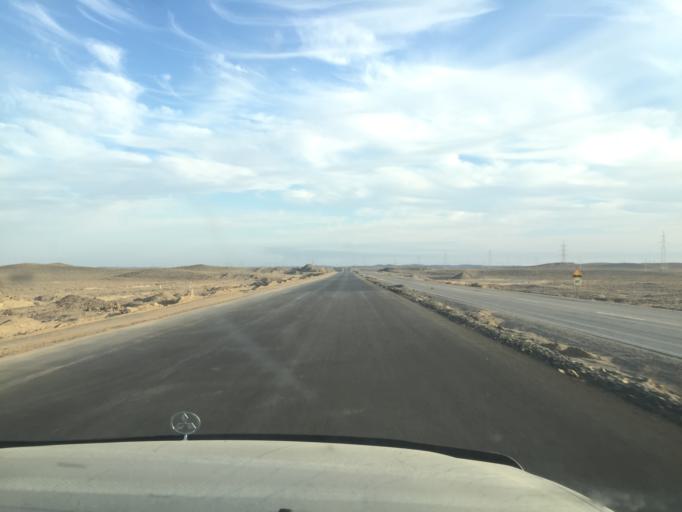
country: KZ
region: Almaty Oblysy
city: Ulken
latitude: 45.2236
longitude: 73.8552
